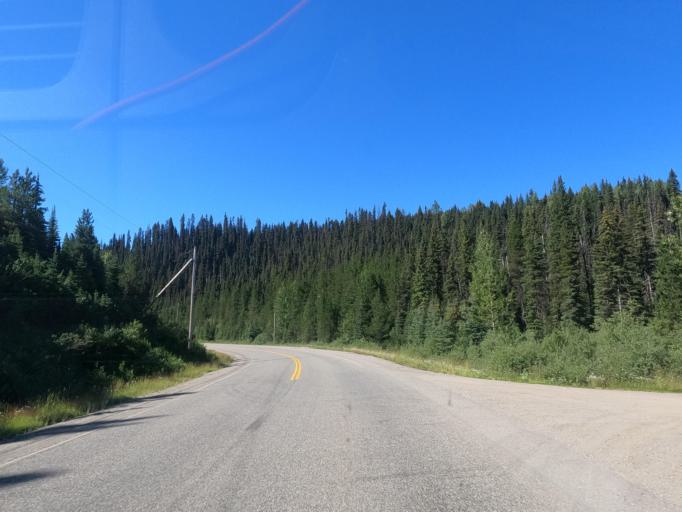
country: CA
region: British Columbia
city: Quesnel
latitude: 53.0844
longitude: -121.6739
